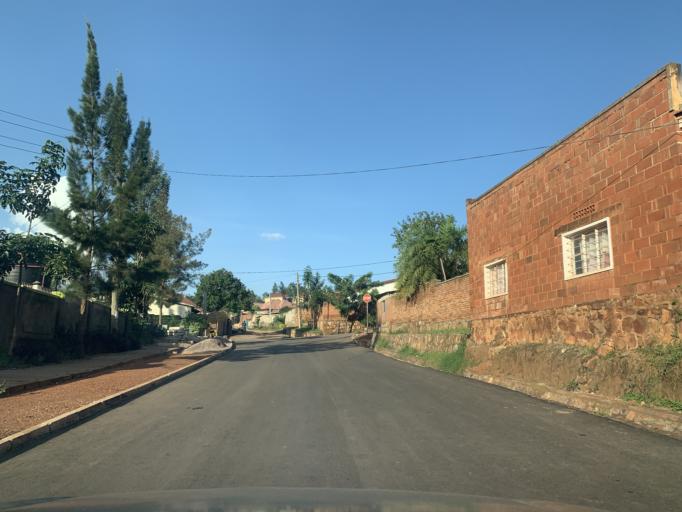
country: RW
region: Kigali
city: Kigali
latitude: -1.9675
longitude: 30.1002
